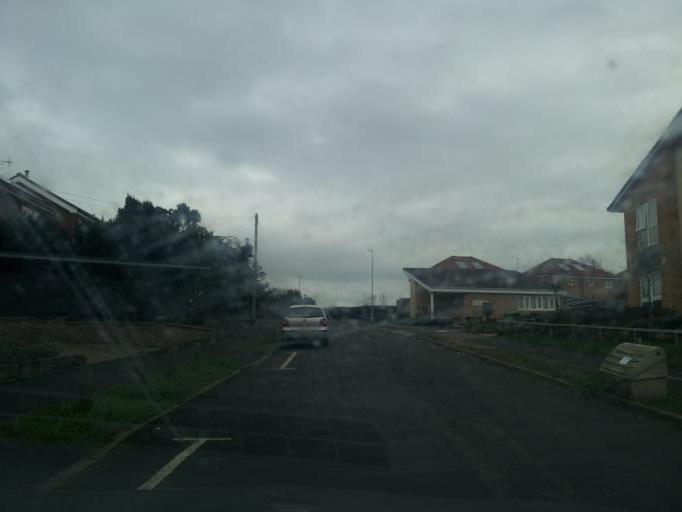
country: GB
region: England
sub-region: Northamptonshire
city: Kettering
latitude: 52.3937
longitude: -0.7003
